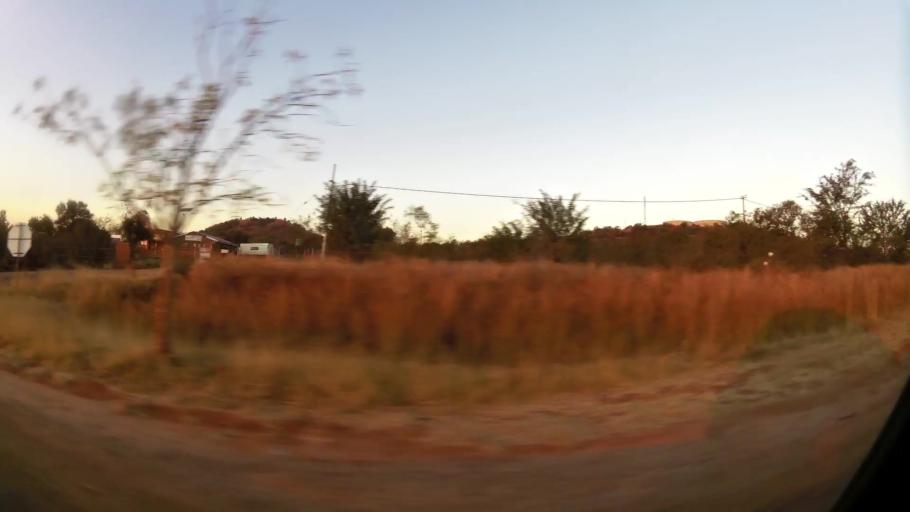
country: ZA
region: North-West
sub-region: Bojanala Platinum District Municipality
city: Rustenburg
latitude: -25.6162
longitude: 27.1796
